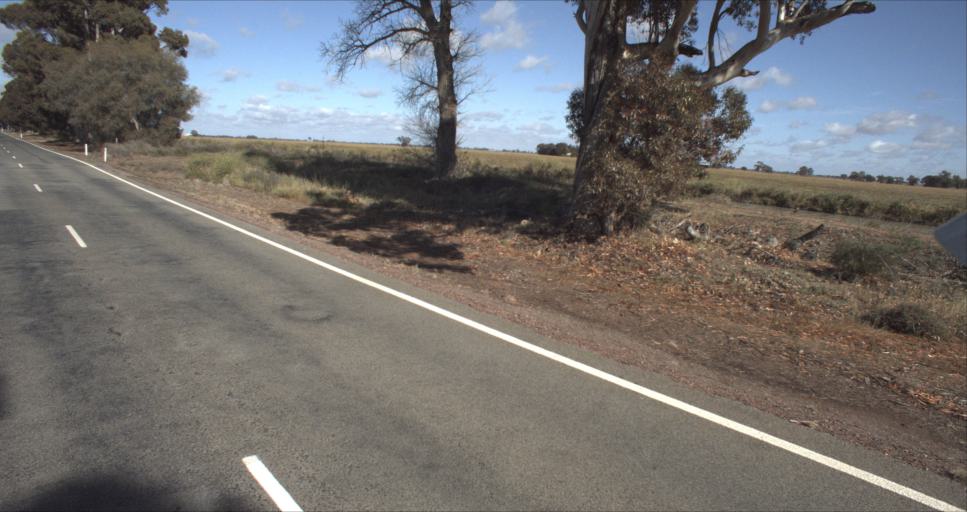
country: AU
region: New South Wales
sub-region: Leeton
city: Leeton
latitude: -34.5474
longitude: 146.3236
